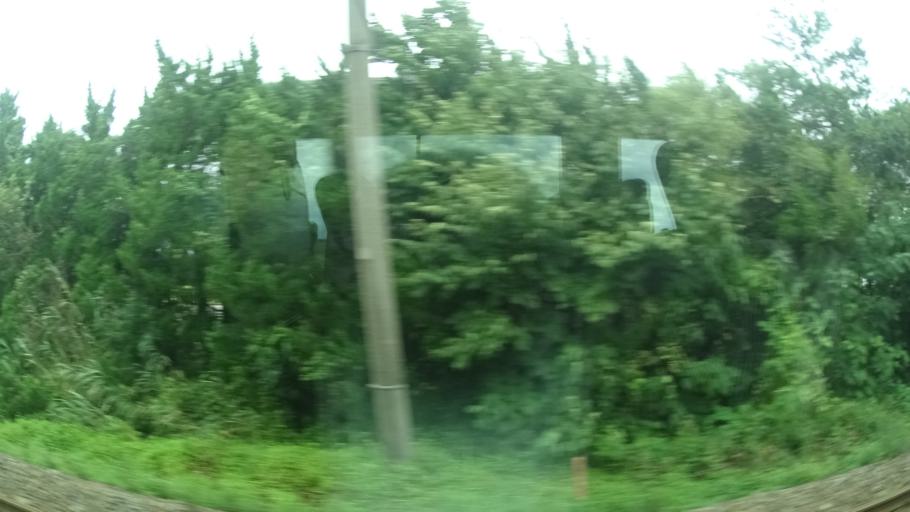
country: JP
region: Niigata
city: Murakami
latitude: 38.1511
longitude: 139.4591
